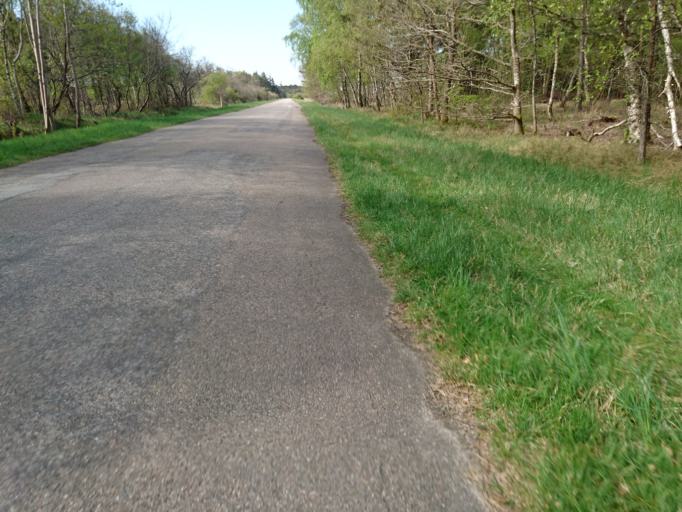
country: DK
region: North Denmark
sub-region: Frederikshavn Kommune
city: Skagen
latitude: 57.7169
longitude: 10.5388
